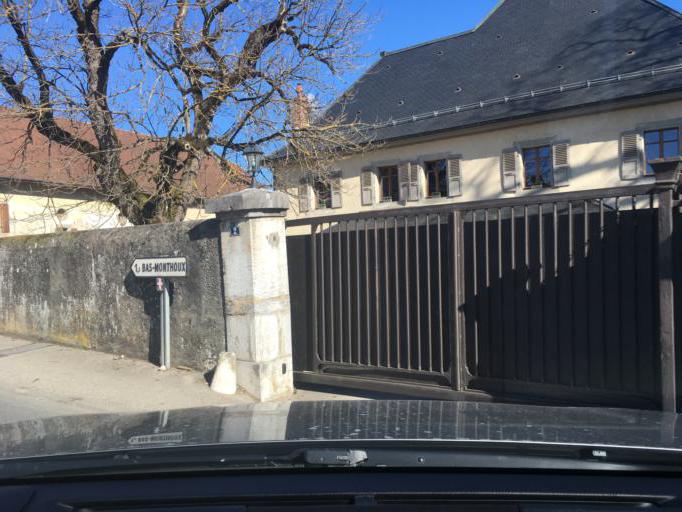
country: FR
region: Rhone-Alpes
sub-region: Departement de la Haute-Savoie
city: Vetraz-Monthoux
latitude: 46.1774
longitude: 6.2684
